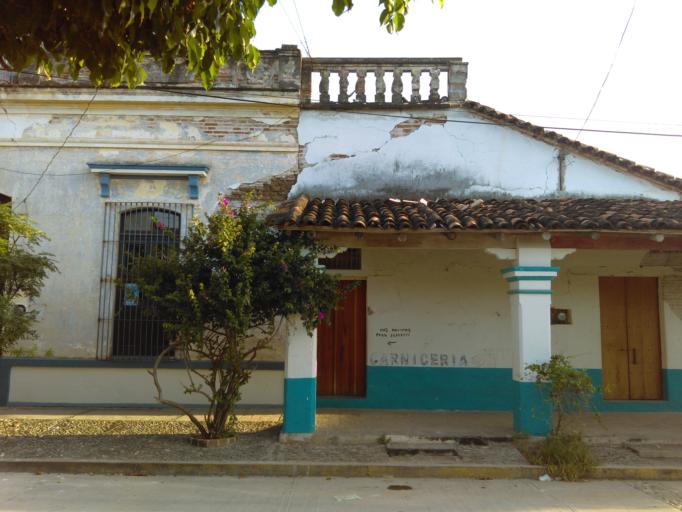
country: MX
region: Oaxaca
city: San Jeronimo Ixtepec
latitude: 16.5679
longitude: -95.0994
